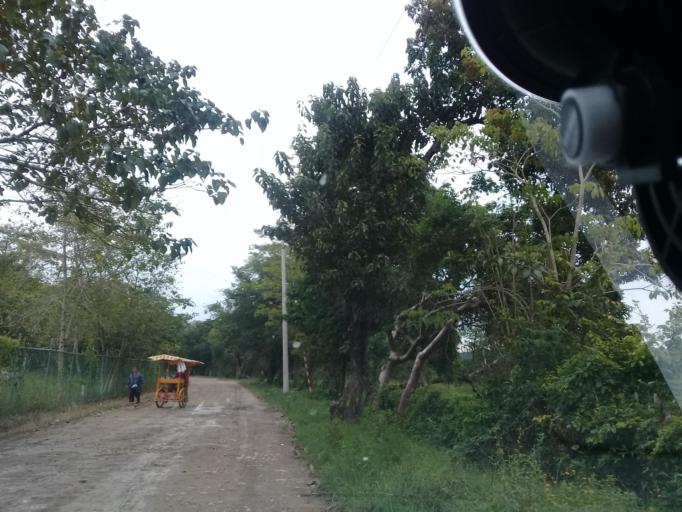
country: MX
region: Hidalgo
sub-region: Huejutla de Reyes
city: Chalahuiyapa
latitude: 21.1629
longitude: -98.3512
